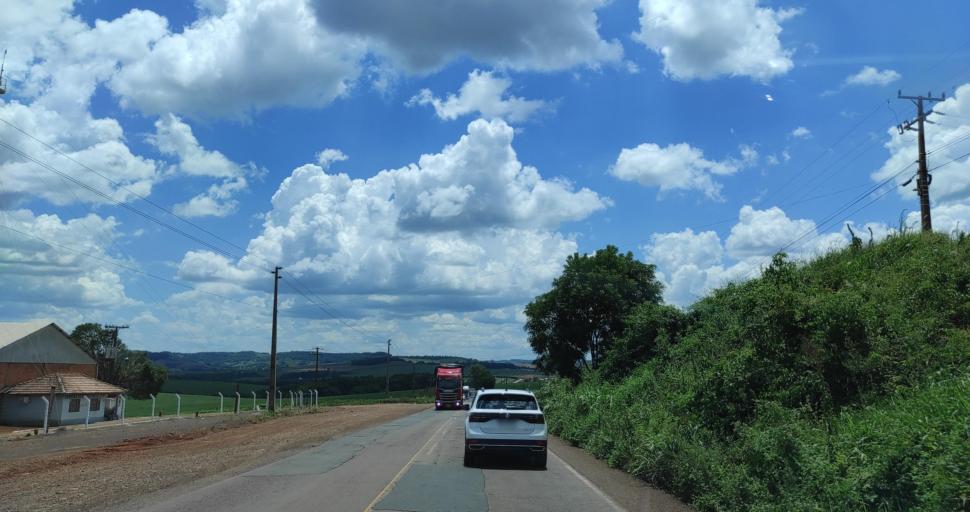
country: BR
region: Santa Catarina
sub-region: Xanxere
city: Xanxere
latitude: -26.7629
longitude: -52.4043
